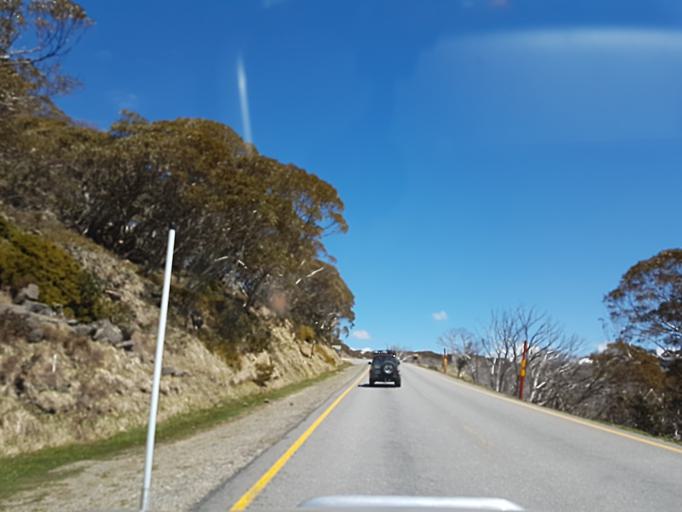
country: AU
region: Victoria
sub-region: Alpine
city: Mount Beauty
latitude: -36.9925
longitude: 147.1562
